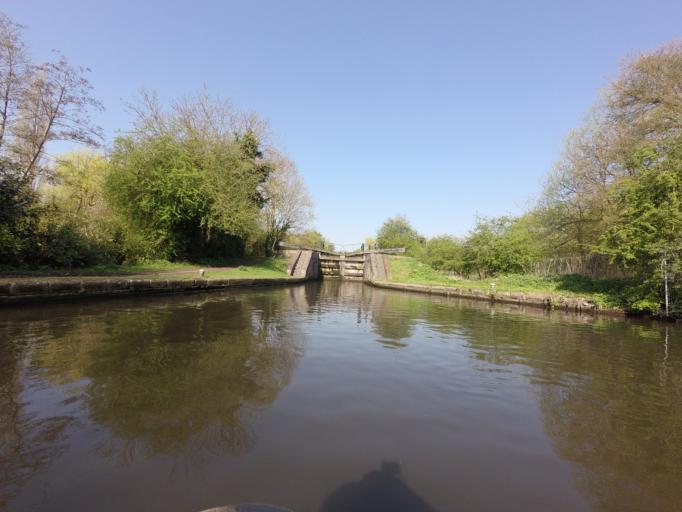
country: GB
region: England
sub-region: Hertfordshire
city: Bovingdon
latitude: 51.7467
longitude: -0.5166
